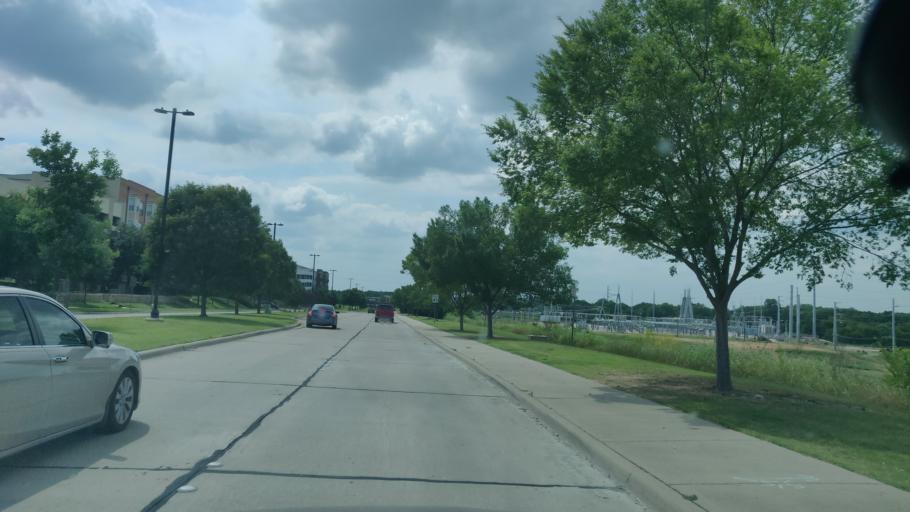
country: US
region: Texas
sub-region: Dallas County
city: Sachse
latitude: 32.9546
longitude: -96.6090
